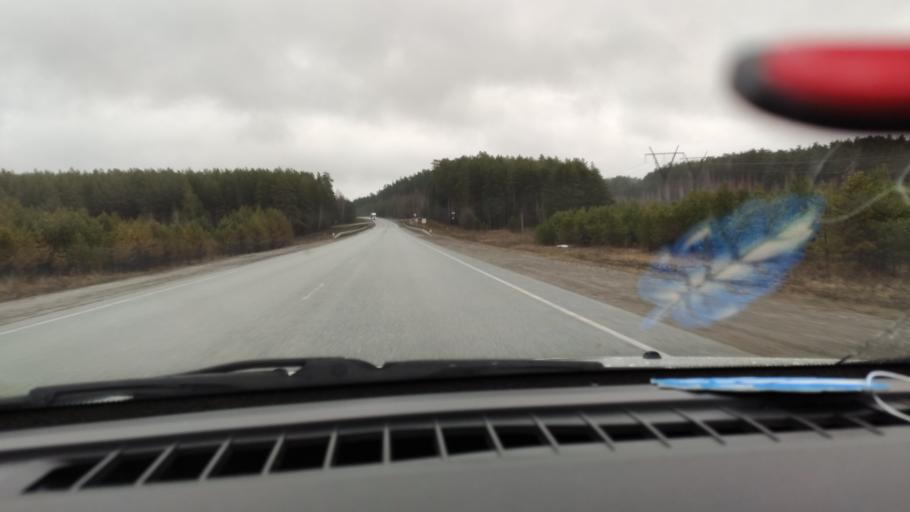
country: RU
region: Sverdlovsk
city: Achit
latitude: 56.7798
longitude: 57.9451
